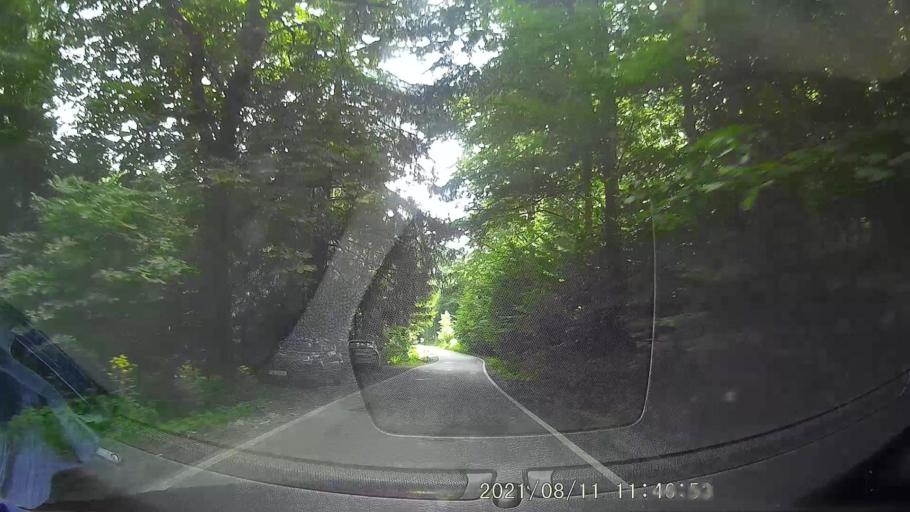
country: PL
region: Lower Silesian Voivodeship
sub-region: Powiat klodzki
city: Stronie Slaskie
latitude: 50.2437
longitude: 16.8497
